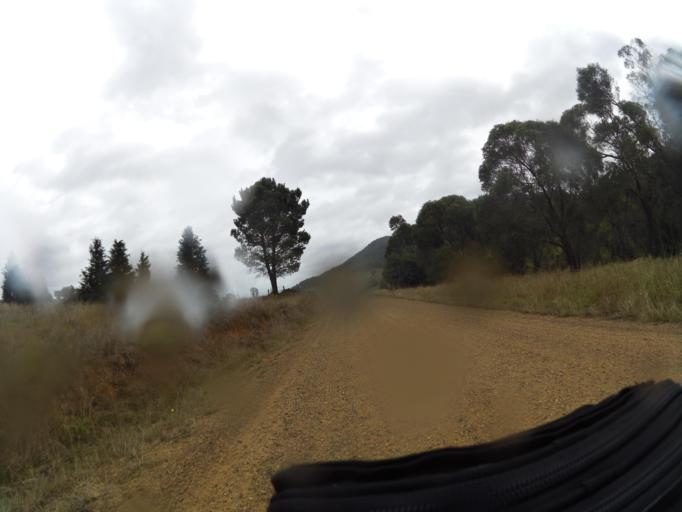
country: AU
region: New South Wales
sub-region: Greater Hume Shire
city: Holbrook
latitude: -36.2383
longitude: 147.6320
